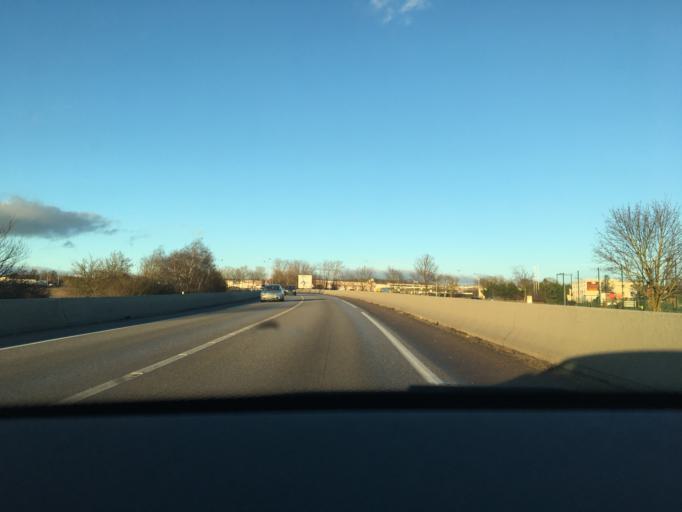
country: FR
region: Ile-de-France
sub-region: Departement des Yvelines
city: Limay
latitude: 48.9891
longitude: 1.7469
